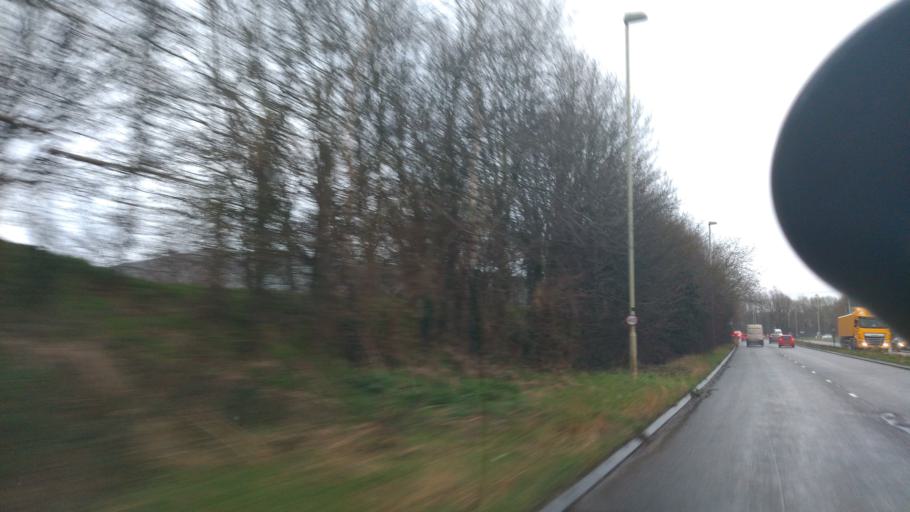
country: GB
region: England
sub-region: Borough of Swindon
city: Broad Blunsdon
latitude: 51.6005
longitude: -1.7802
